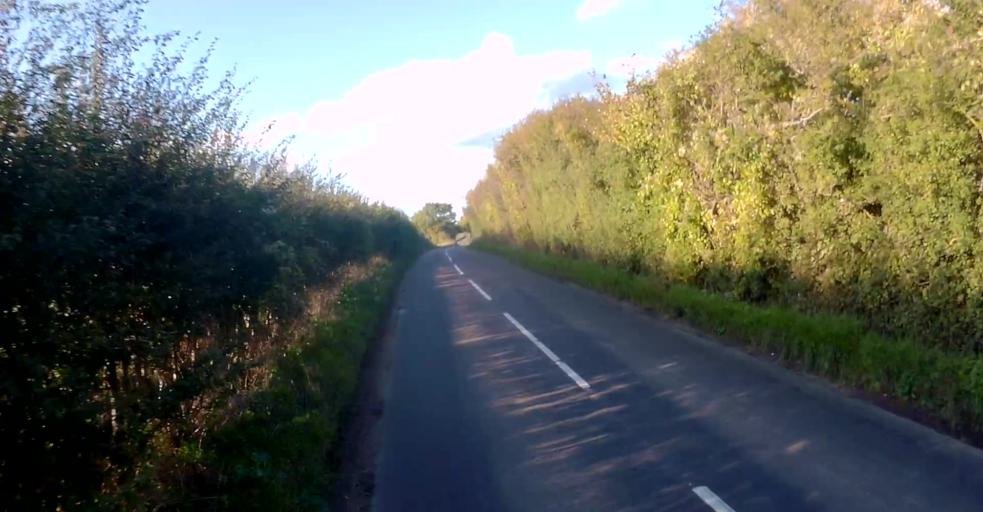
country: GB
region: England
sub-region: Hampshire
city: Odiham
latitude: 51.2422
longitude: -0.9314
